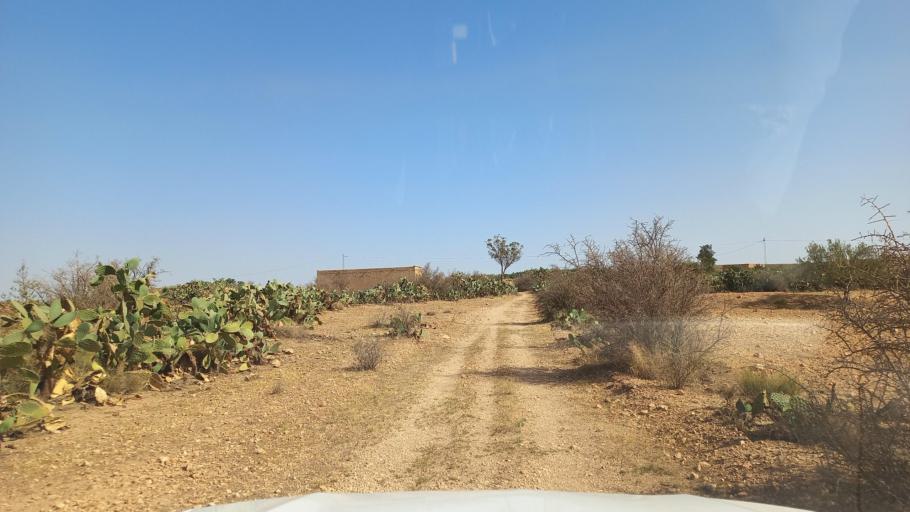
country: TN
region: Al Qasrayn
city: Kasserine
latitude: 35.2128
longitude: 8.9858
